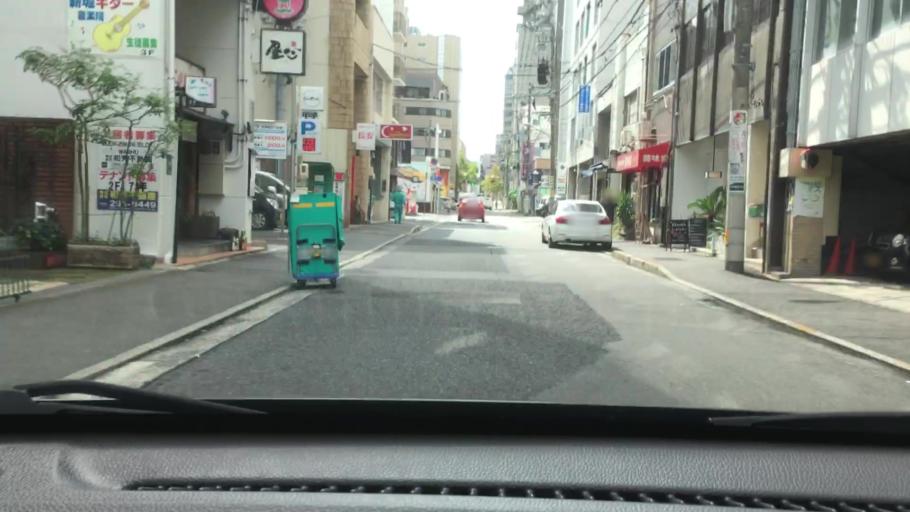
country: JP
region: Hiroshima
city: Hiroshima-shi
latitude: 34.3923
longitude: 132.4553
